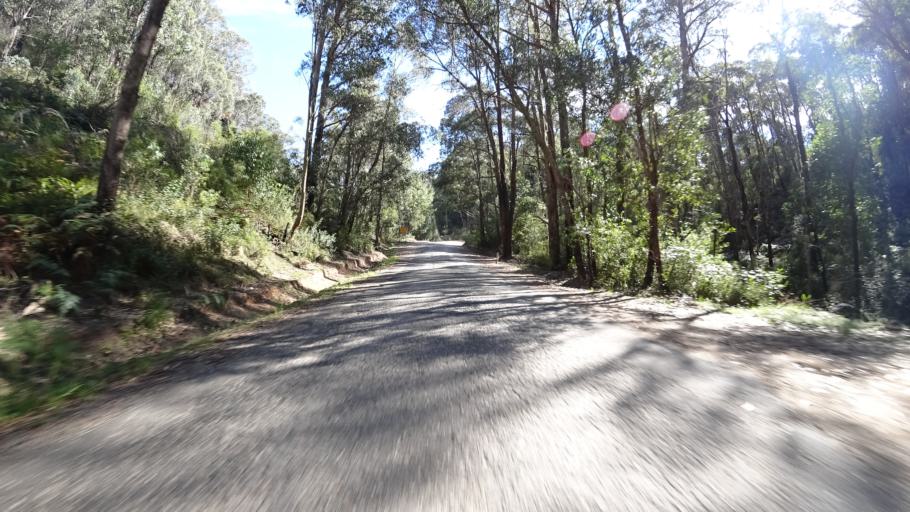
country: AU
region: New South Wales
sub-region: Lithgow
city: Lithgow
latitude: -33.4488
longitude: 150.1759
